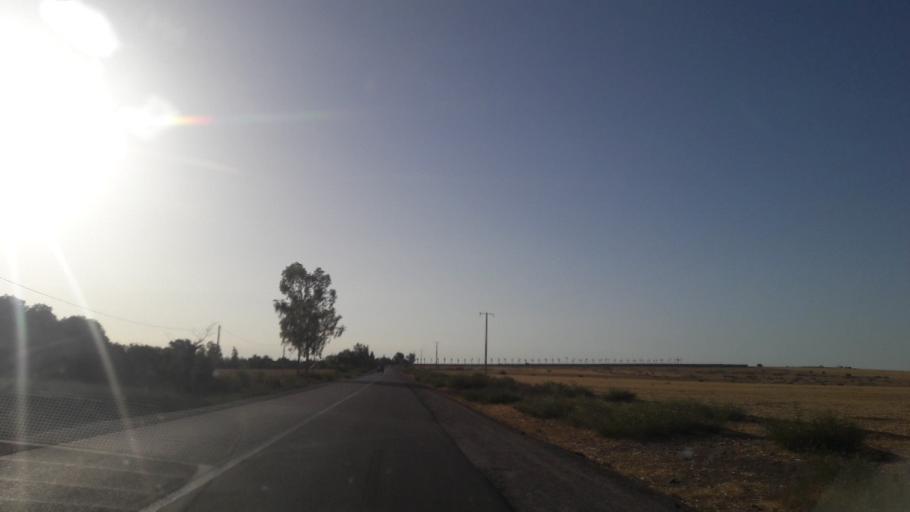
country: MA
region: Chaouia-Ouardigha
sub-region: Khouribga Province
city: Boujniba
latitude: 32.9727
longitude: -6.6683
